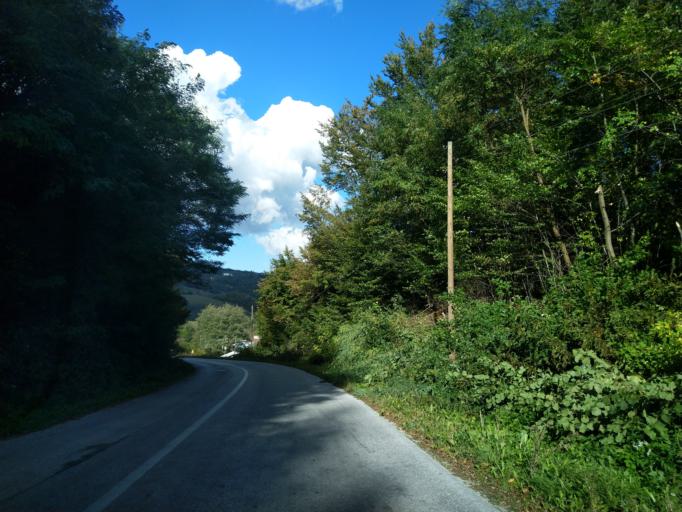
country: RS
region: Central Serbia
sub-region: Zlatiborski Okrug
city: Uzice
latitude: 43.8849
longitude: 19.7761
